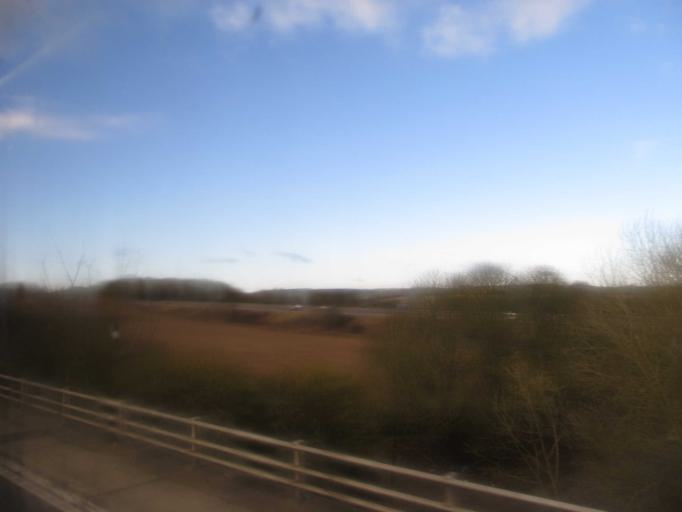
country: GB
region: England
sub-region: Hampshire
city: Overton
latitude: 51.2046
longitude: -1.1827
